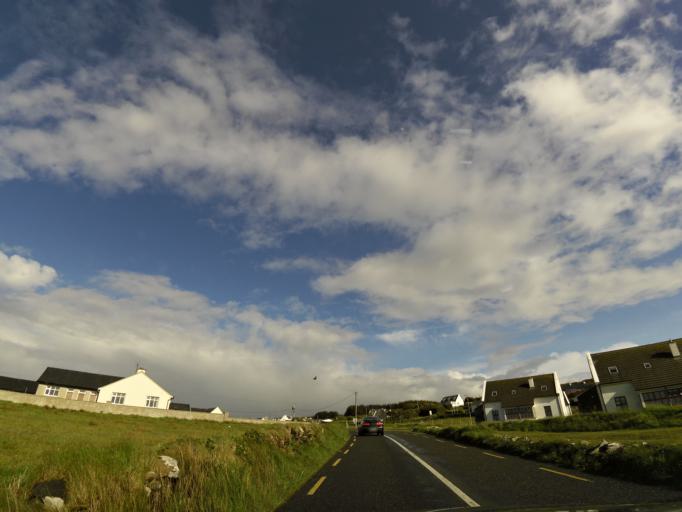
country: IE
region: Connaught
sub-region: County Galway
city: Bearna
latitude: 53.0087
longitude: -9.3572
